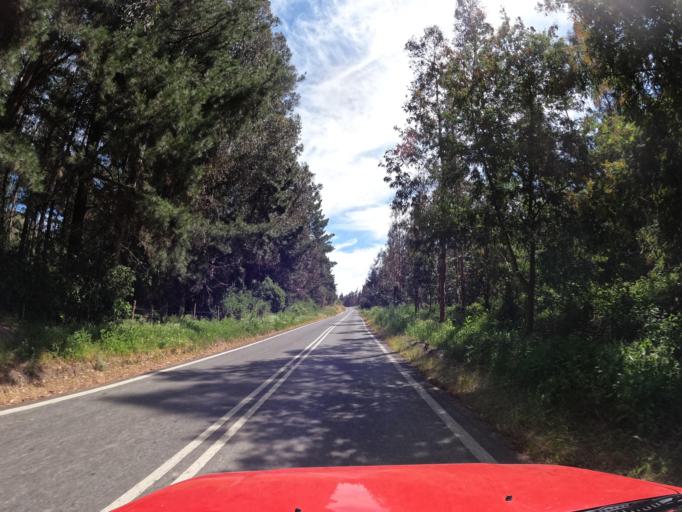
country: CL
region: Maule
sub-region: Provincia de Talca
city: Talca
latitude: -34.9930
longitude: -71.8719
